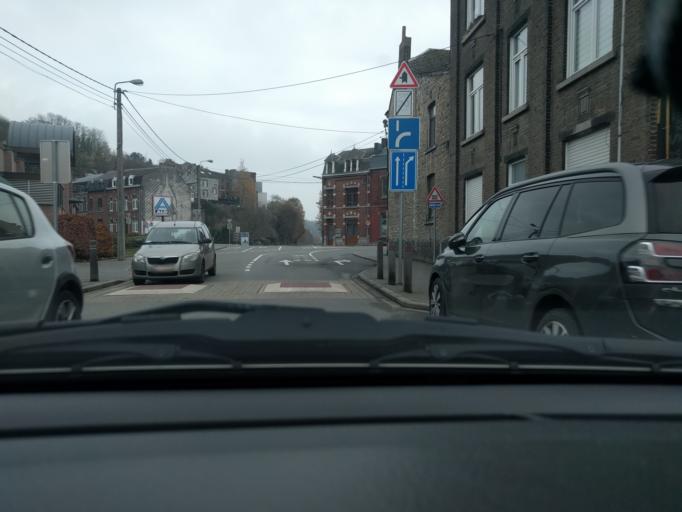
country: BE
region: Wallonia
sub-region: Province de Namur
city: Namur
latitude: 50.4685
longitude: 4.8811
